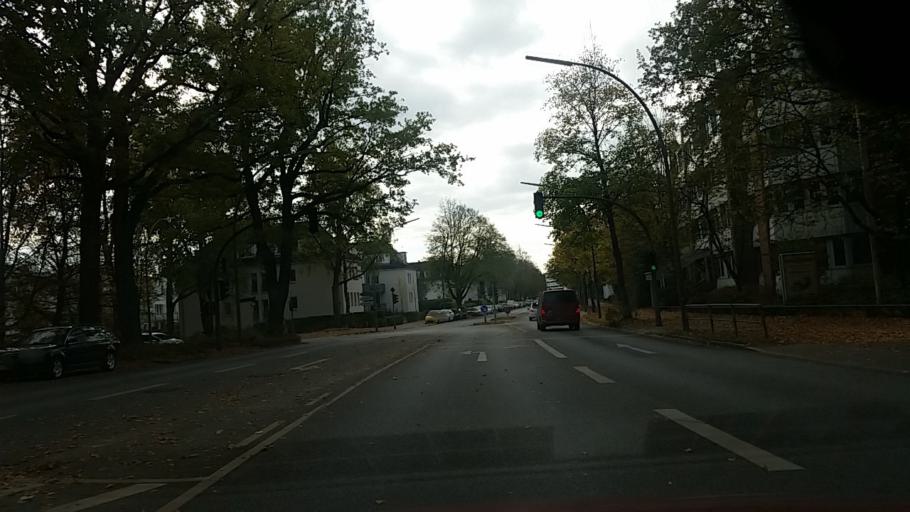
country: DE
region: Hamburg
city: Fuhlsbuettel
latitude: 53.6537
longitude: 10.0196
